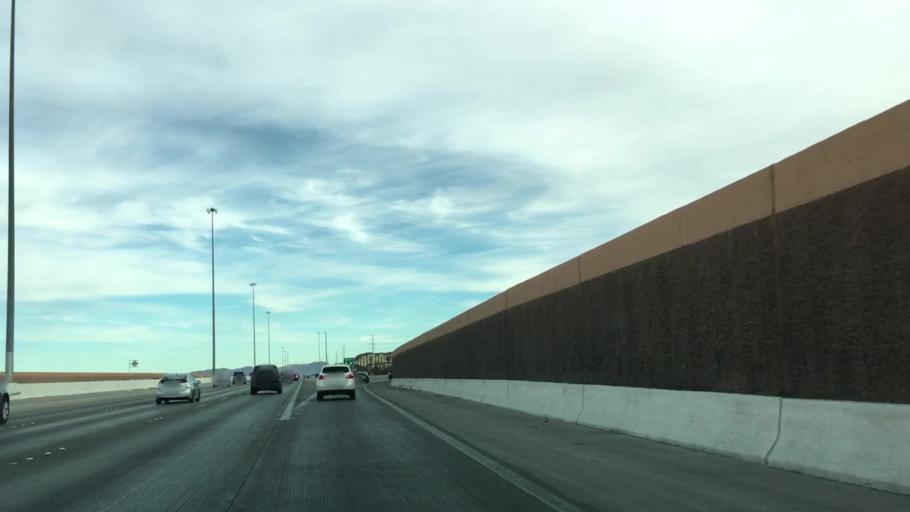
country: US
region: Nevada
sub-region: Clark County
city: Whitney
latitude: 36.0234
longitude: -115.1055
